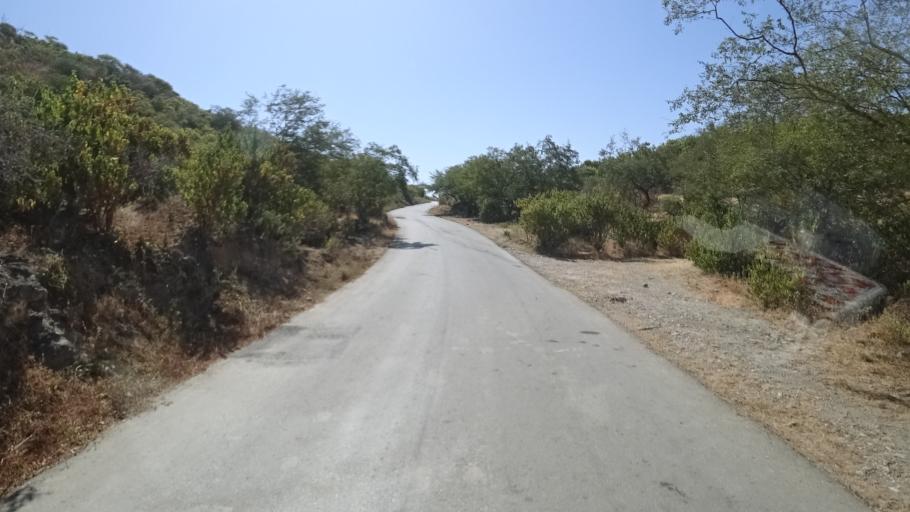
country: OM
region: Zufar
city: Salalah
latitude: 17.0747
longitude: 54.4400
